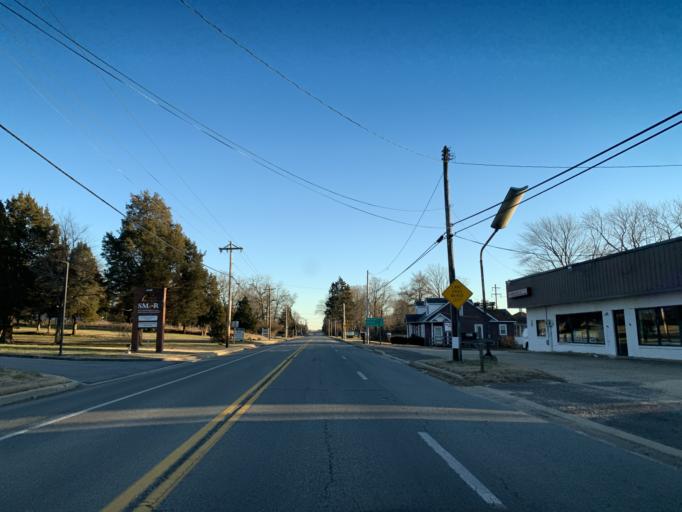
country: US
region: Maryland
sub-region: Charles County
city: Hughesville
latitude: 38.5321
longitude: -76.7836
